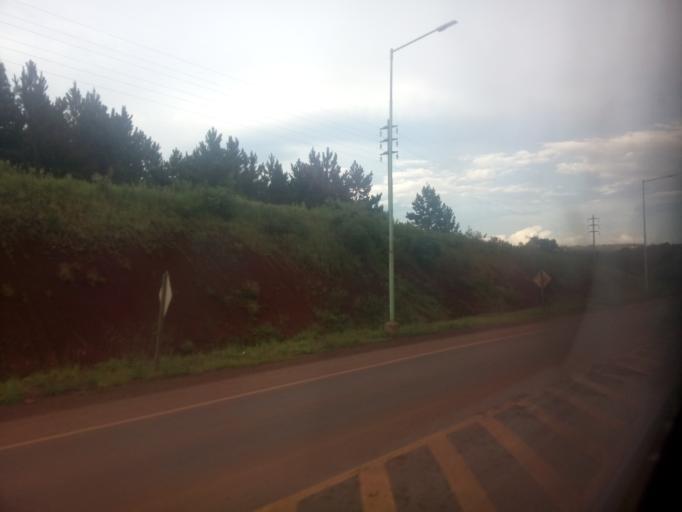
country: AR
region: Misiones
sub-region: Departamento de Obera
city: Obera
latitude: -27.5094
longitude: -55.1356
